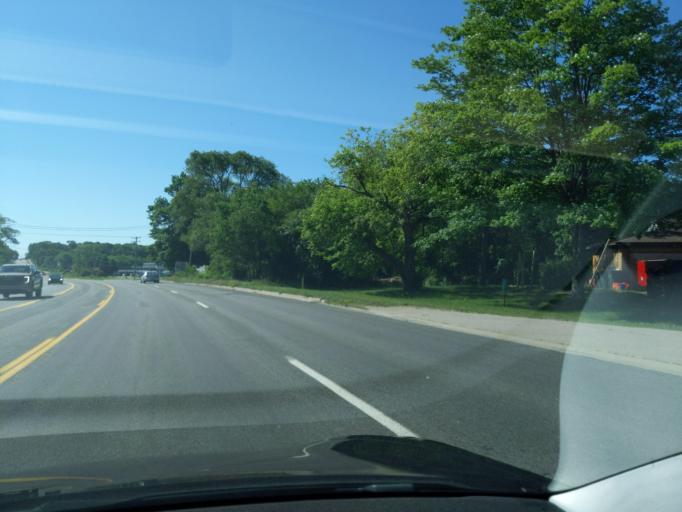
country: US
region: Michigan
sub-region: Muskegon County
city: North Muskegon
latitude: 43.2752
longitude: -86.2610
